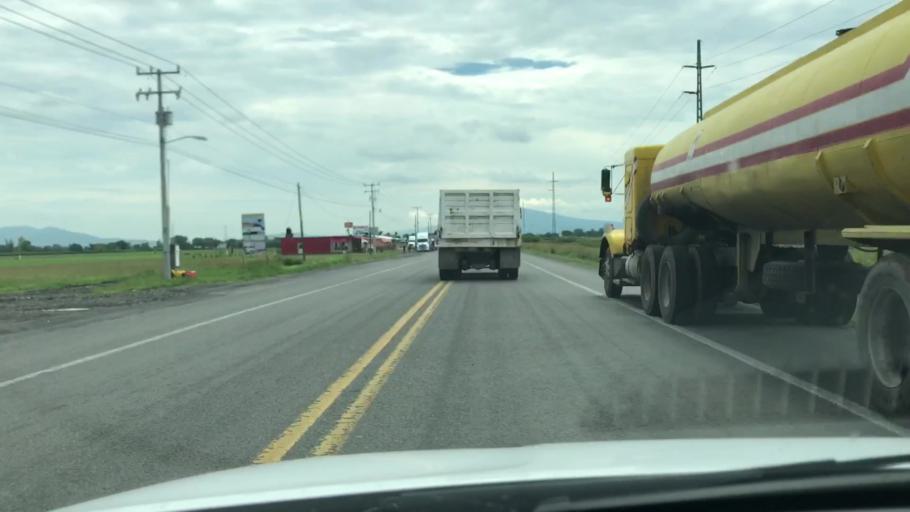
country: MX
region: Michoacan
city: Tanhuato de Guerrero
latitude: 20.2794
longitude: -102.3637
